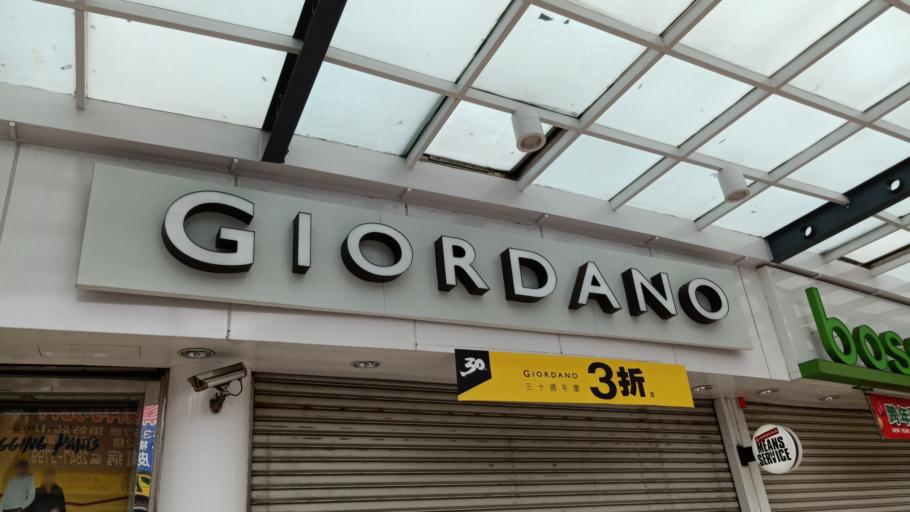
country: TW
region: Taipei
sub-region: Taipei
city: Banqiao
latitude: 25.0821
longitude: 121.4639
